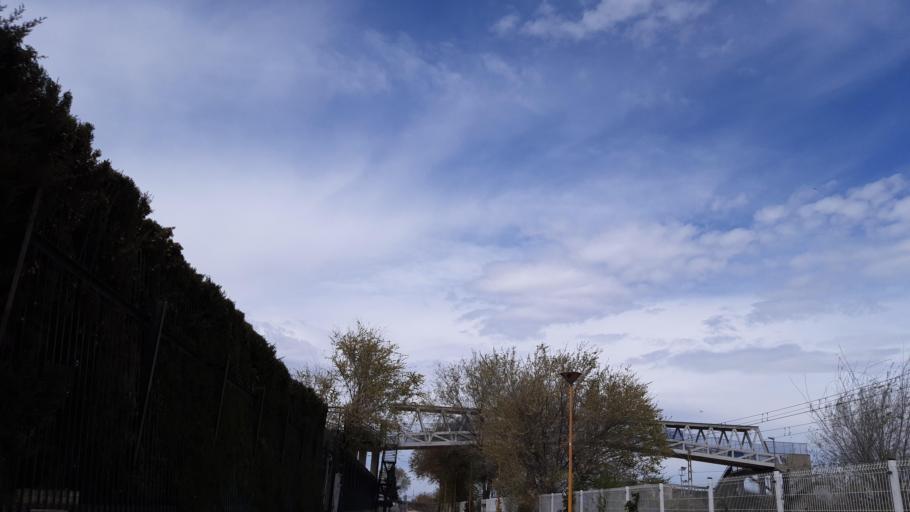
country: ES
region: Aragon
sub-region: Provincia de Zaragoza
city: Utebo
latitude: 41.7118
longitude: -1.0003
